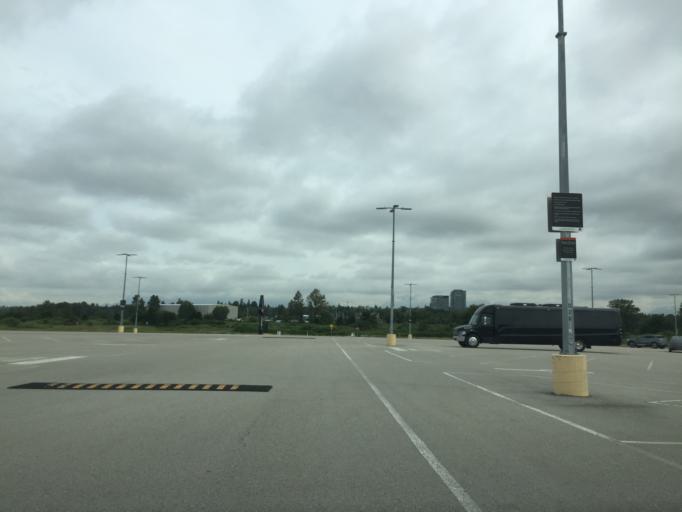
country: CA
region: British Columbia
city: Richmond
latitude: 49.1979
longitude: -123.1447
